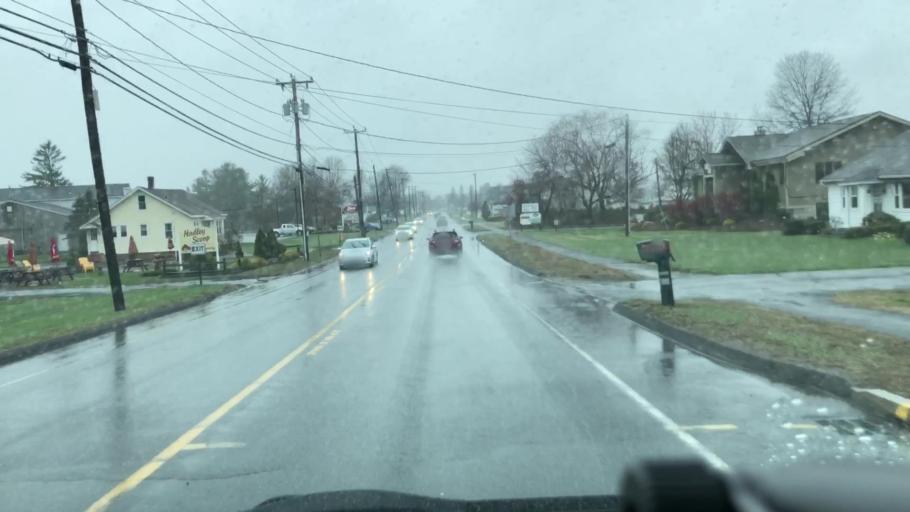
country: US
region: Massachusetts
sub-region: Hampshire County
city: Hadley
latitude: 42.3467
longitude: -72.5734
